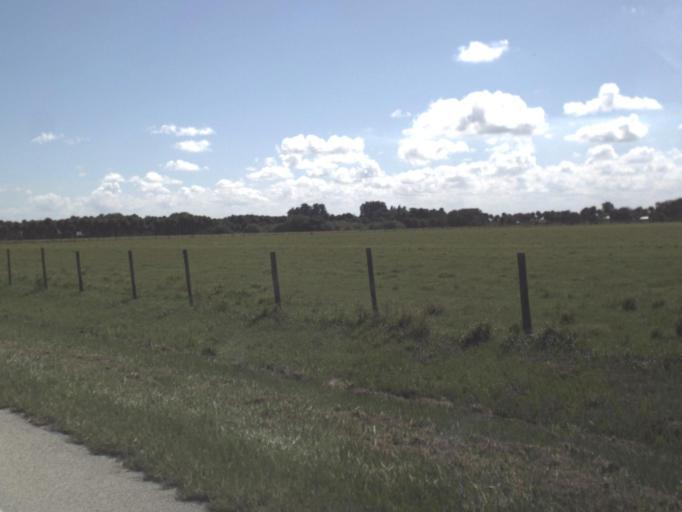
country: US
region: Florida
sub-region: Hendry County
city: Port LaBelle
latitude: 26.8123
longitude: -81.2546
